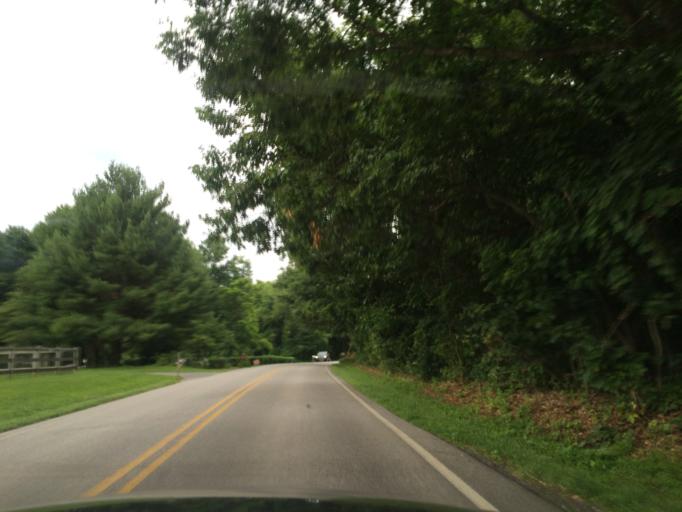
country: US
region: Maryland
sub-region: Howard County
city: Highland
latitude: 39.2284
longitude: -76.9954
